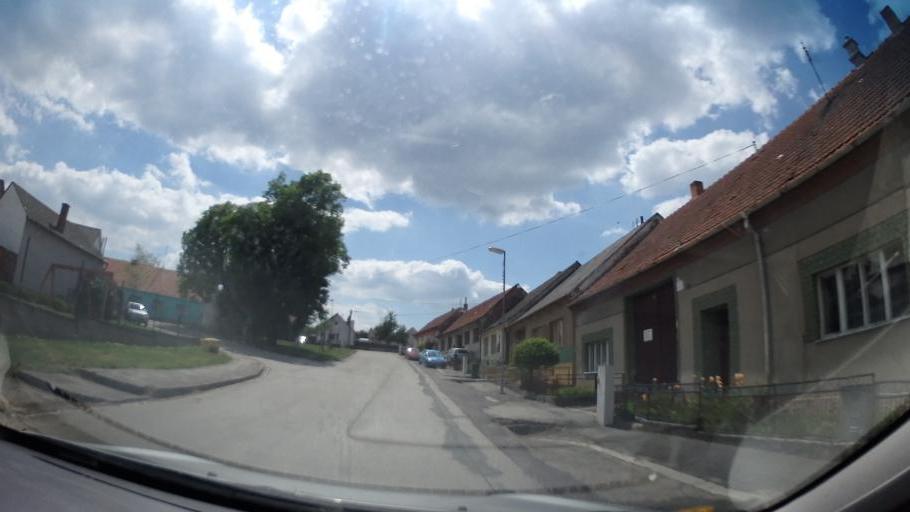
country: CZ
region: Vysocina
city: Mohelno
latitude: 49.1145
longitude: 16.1883
